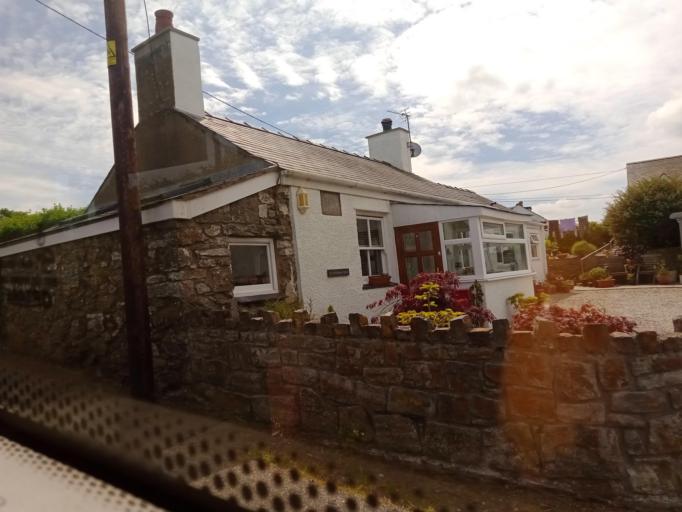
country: GB
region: Wales
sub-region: Anglesey
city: Beaumaris
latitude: 53.2954
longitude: -4.1378
